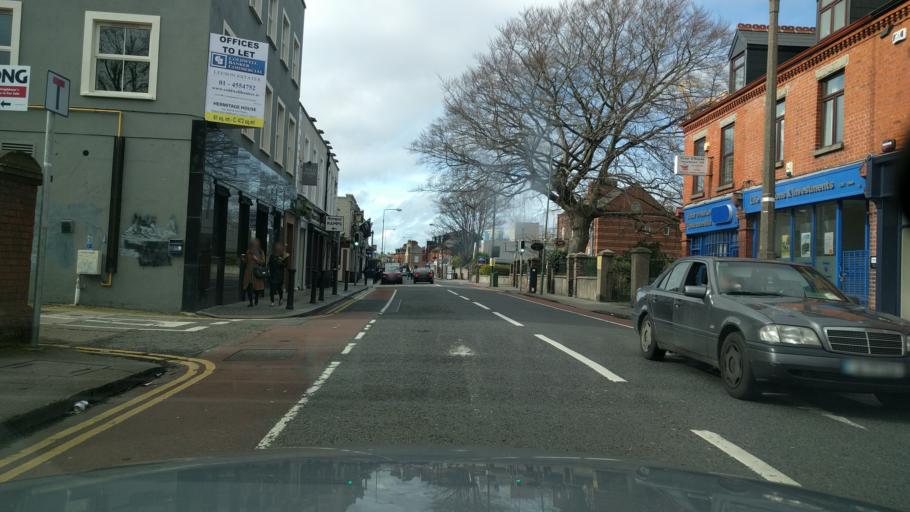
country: IE
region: Leinster
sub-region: Dublin City
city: Dublin
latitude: 53.3231
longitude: -6.2495
